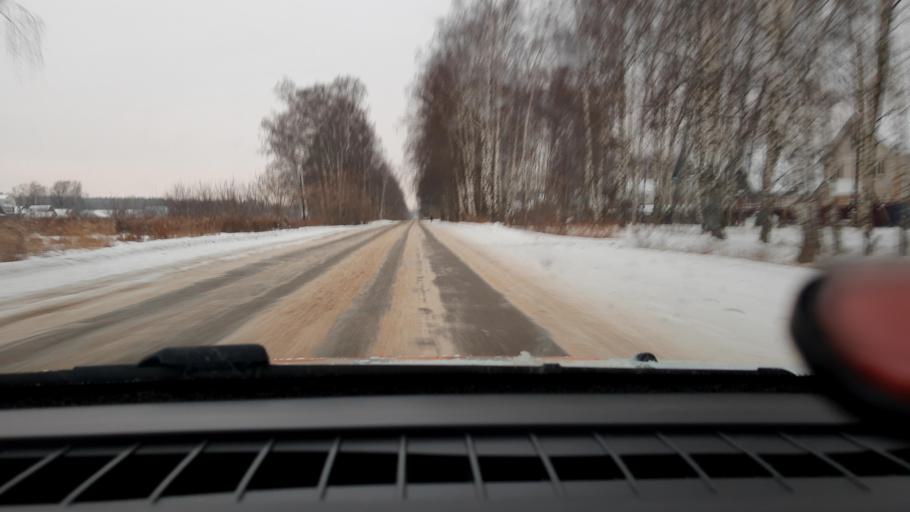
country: RU
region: Nizjnij Novgorod
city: Pamyat' Parizhskoy Kommuny
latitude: 56.2706
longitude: 44.4172
